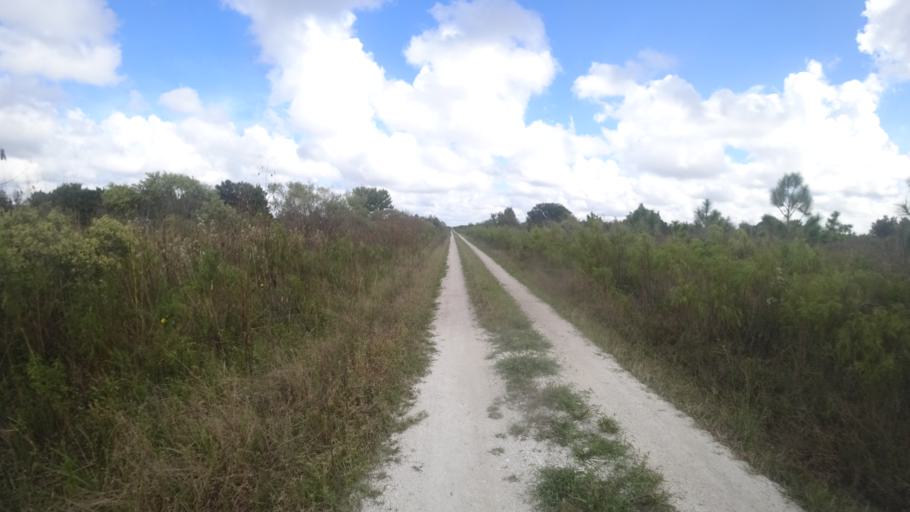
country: US
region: Florida
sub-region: Hillsborough County
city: Wimauma
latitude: 27.4996
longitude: -82.1495
